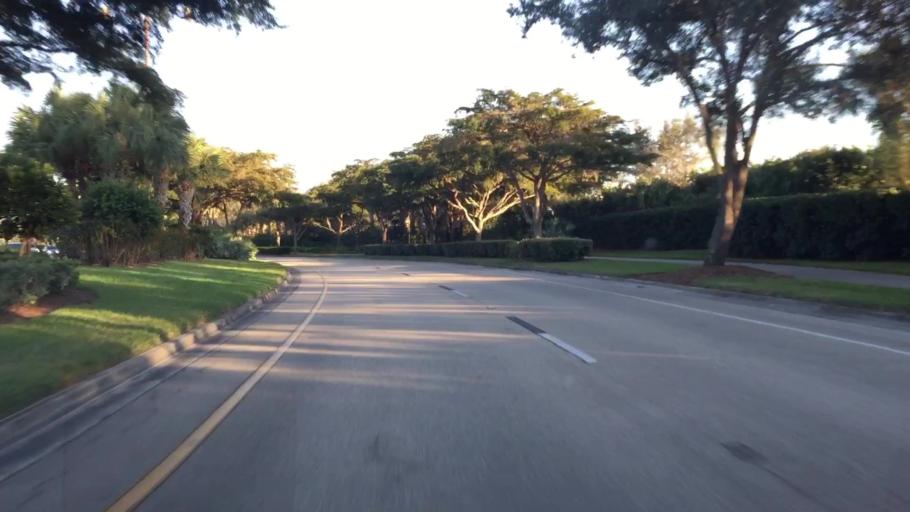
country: US
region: Florida
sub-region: Lee County
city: Estero
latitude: 26.3952
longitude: -81.7940
